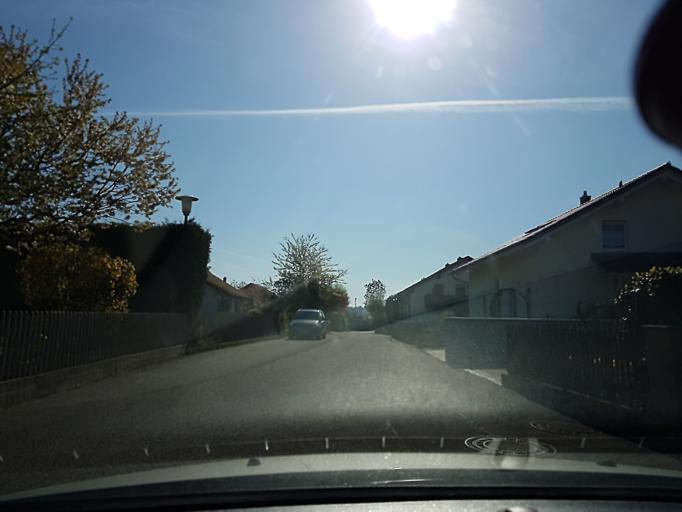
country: DE
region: Bavaria
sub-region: Lower Bavaria
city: Furth
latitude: 48.4072
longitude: 12.3921
